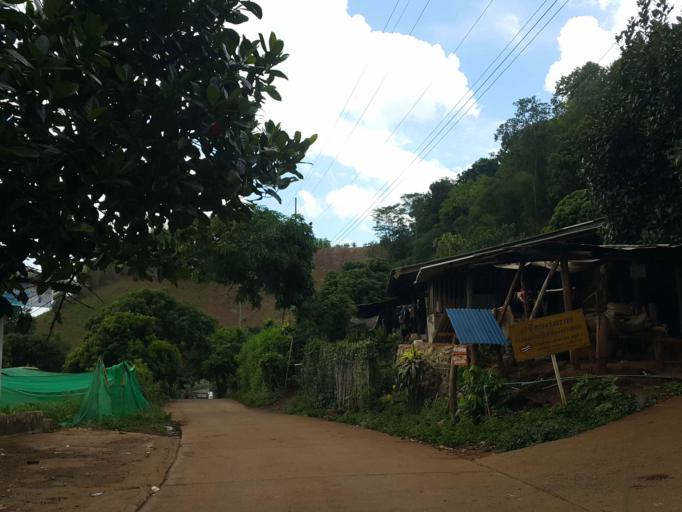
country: TH
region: Chiang Mai
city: Samoeng
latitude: 18.7825
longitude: 98.8255
